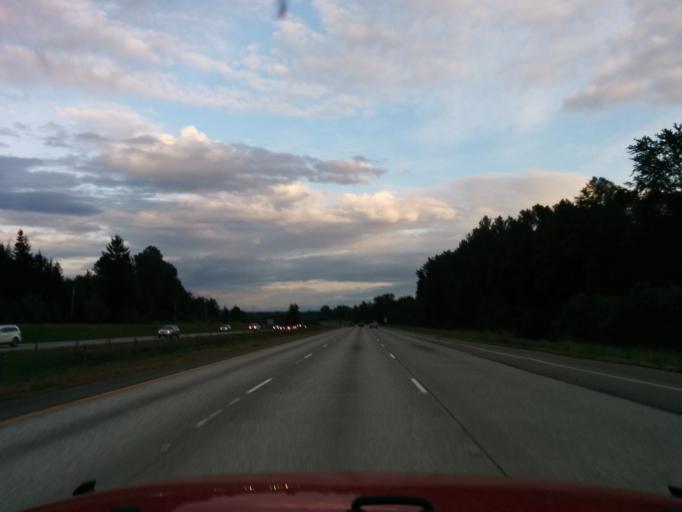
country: US
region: Washington
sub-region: Snohomish County
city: Bryant
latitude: 48.2346
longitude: -122.2372
